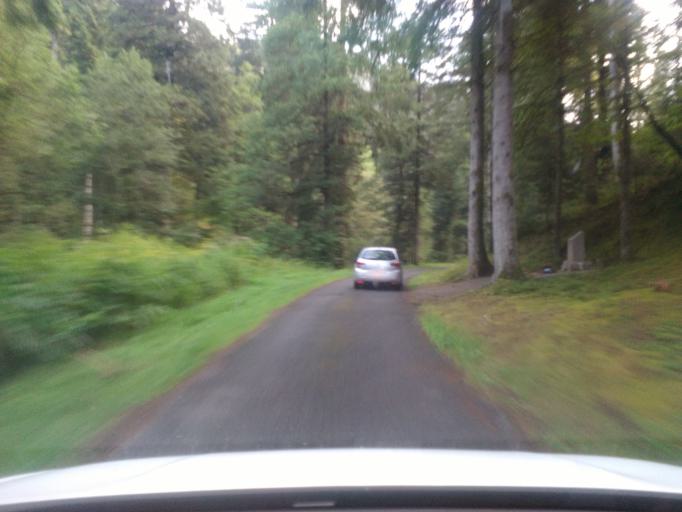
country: FR
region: Lorraine
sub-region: Departement des Vosges
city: Moyenmoutier
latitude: 48.4113
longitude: 6.9195
